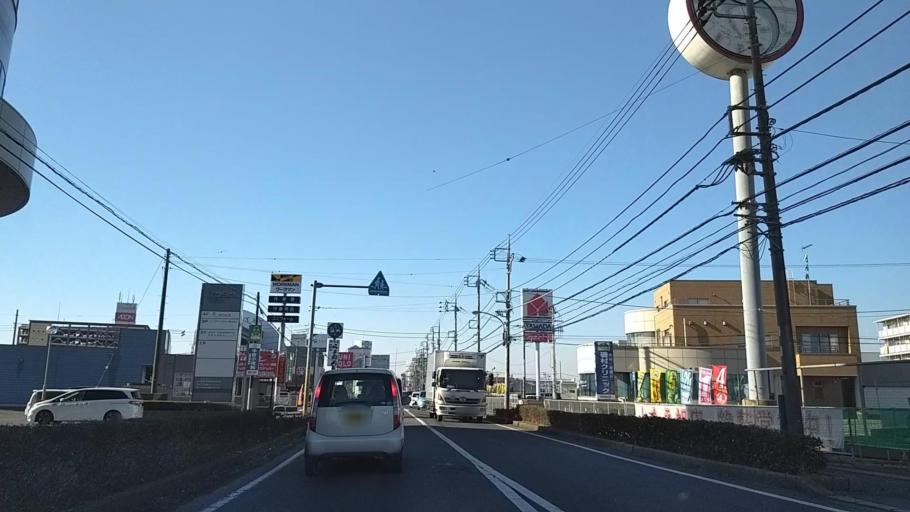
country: JP
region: Chiba
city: Asahi
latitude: 35.7263
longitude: 140.6636
